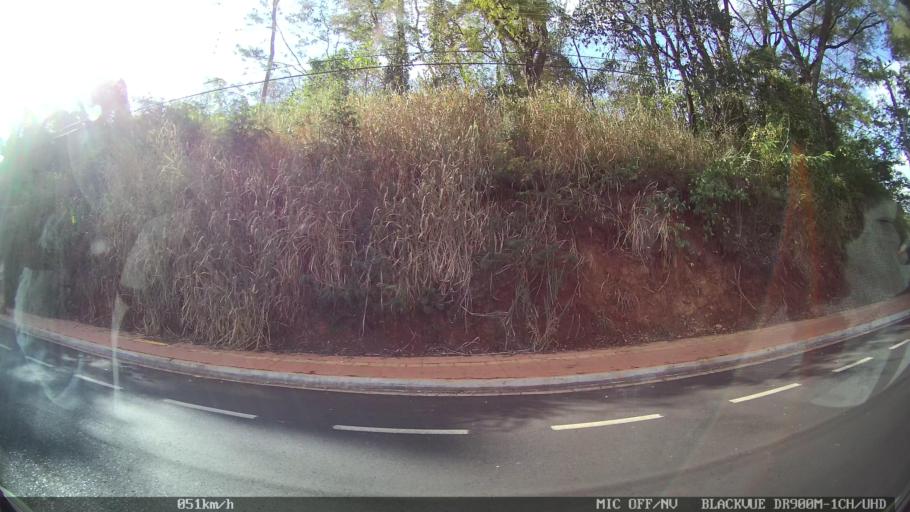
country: BR
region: Sao Paulo
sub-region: Ribeirao Preto
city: Ribeirao Preto
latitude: -21.1743
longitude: -47.8401
